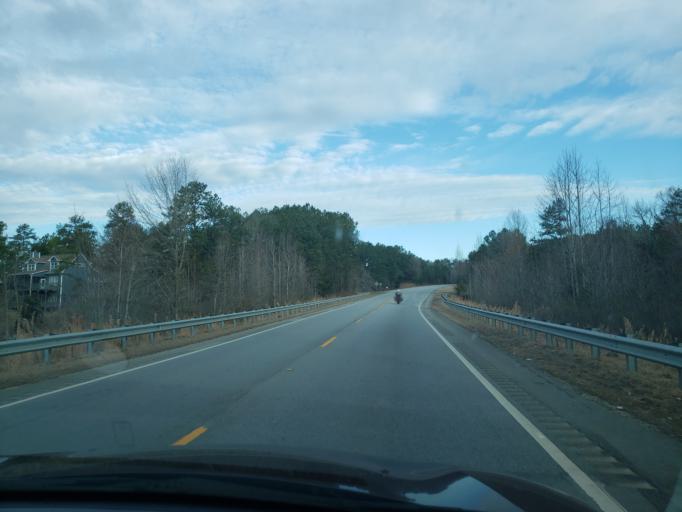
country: US
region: Alabama
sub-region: Randolph County
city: Wedowee
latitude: 33.3281
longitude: -85.4885
